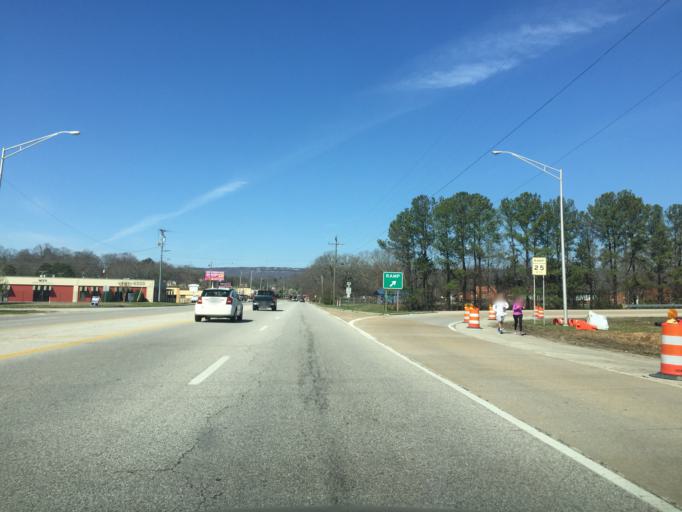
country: US
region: Tennessee
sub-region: Hamilton County
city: Red Bank
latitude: 35.1122
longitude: -85.2518
